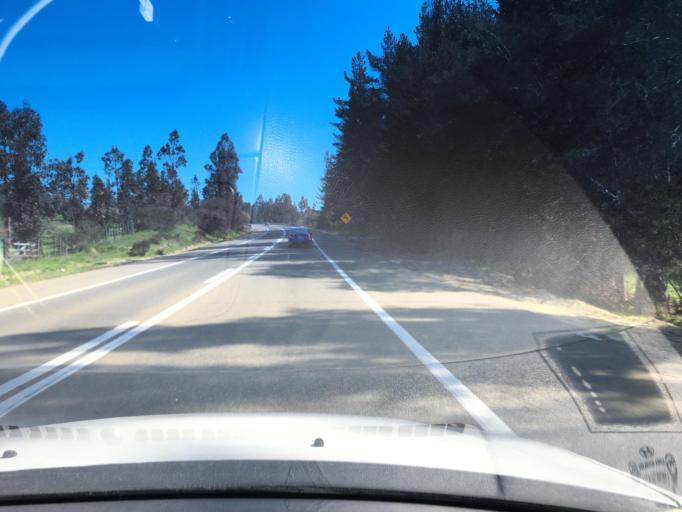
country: CL
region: Valparaiso
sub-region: San Antonio Province
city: El Tabo
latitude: -33.3908
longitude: -71.4779
